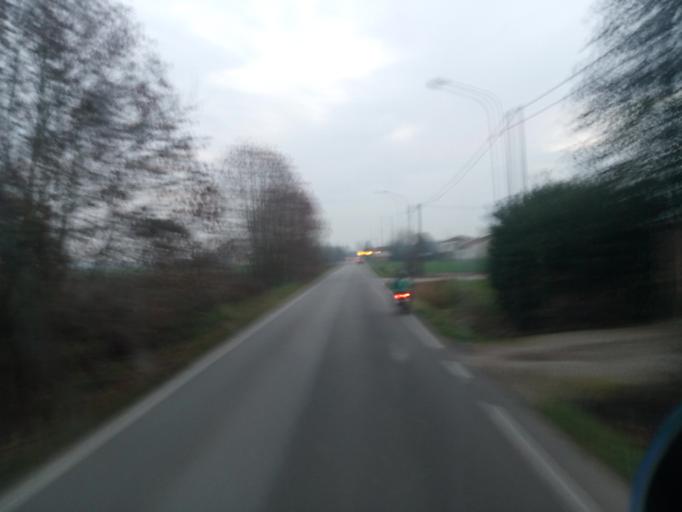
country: IT
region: Lombardy
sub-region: Provincia di Mantova
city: Roncoferraro
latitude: 45.1444
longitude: 10.9294
